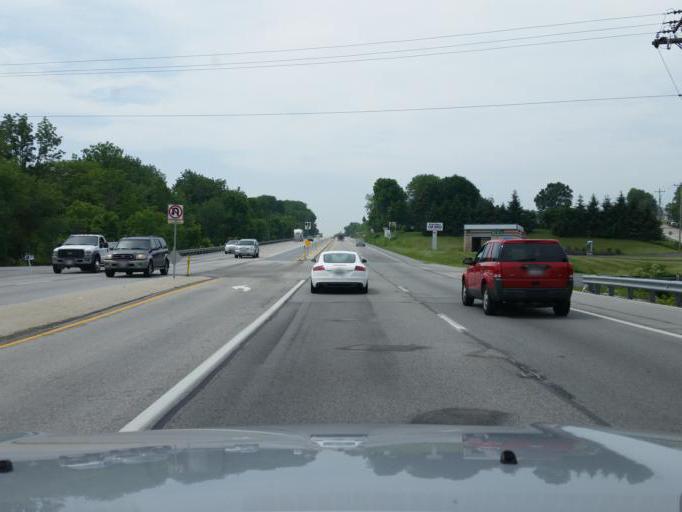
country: US
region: Pennsylvania
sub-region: York County
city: Dillsburg
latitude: 40.1029
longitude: -77.0430
